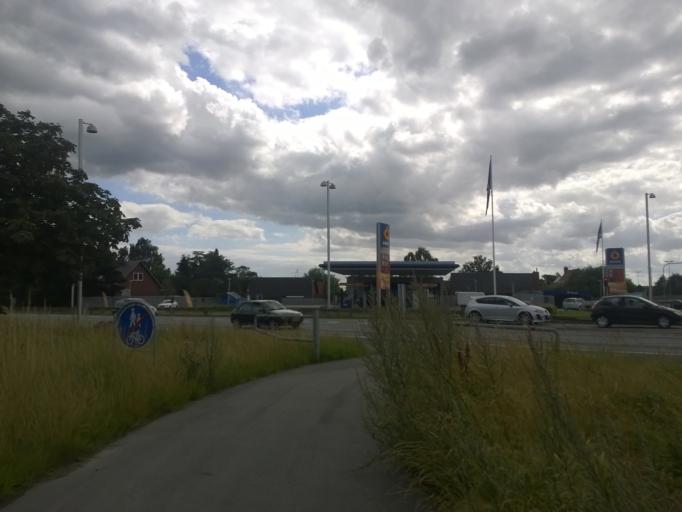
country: DK
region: Capital Region
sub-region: Ballerup Kommune
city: Ballerup
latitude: 55.7320
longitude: 12.3751
